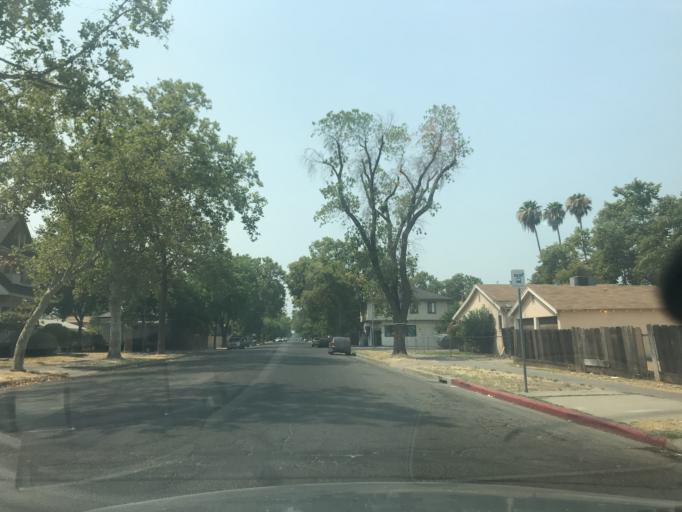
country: US
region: California
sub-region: Merced County
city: Merced
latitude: 37.3076
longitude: -120.4781
